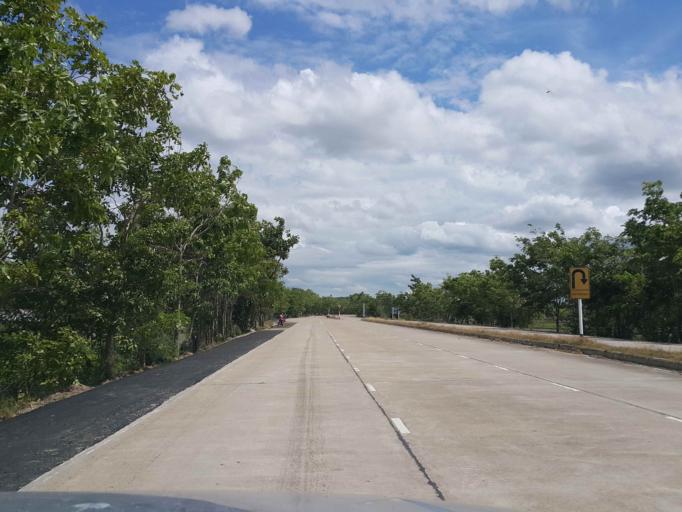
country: TH
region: Tak
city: Tak
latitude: 16.8736
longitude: 99.1122
